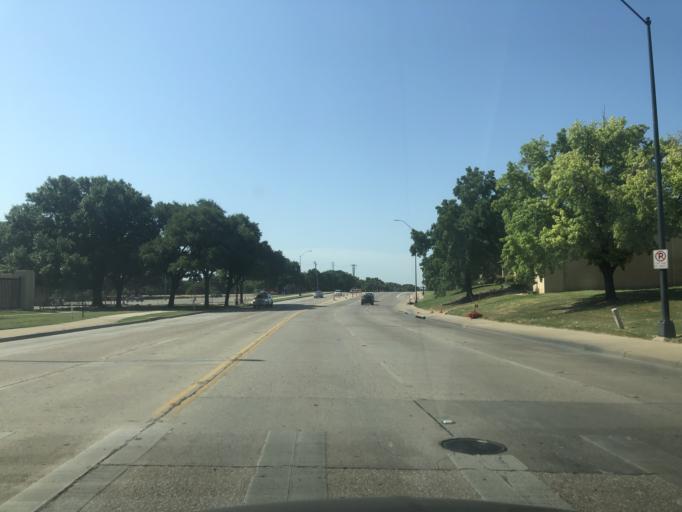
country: US
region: Texas
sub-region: Tarrant County
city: River Oaks
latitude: 32.7458
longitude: -97.3618
